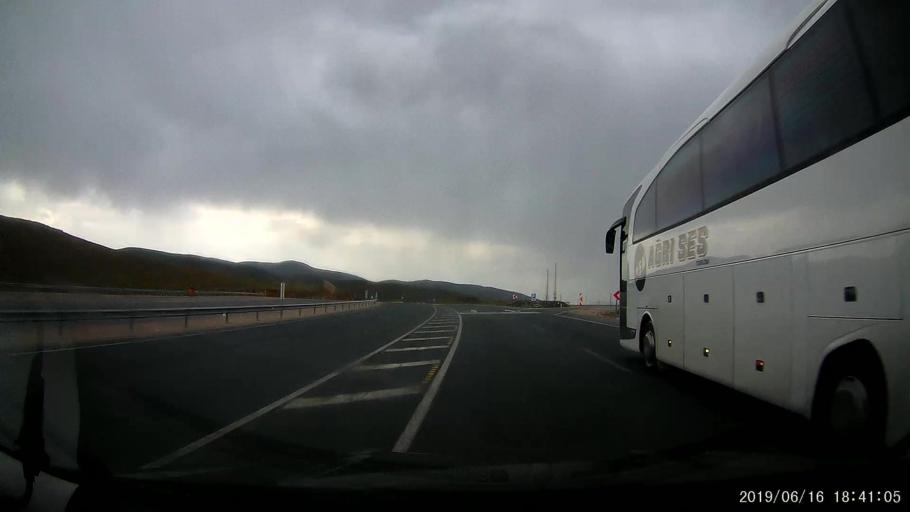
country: TR
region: Erzincan
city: Catalarmut
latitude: 39.8777
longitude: 39.1334
